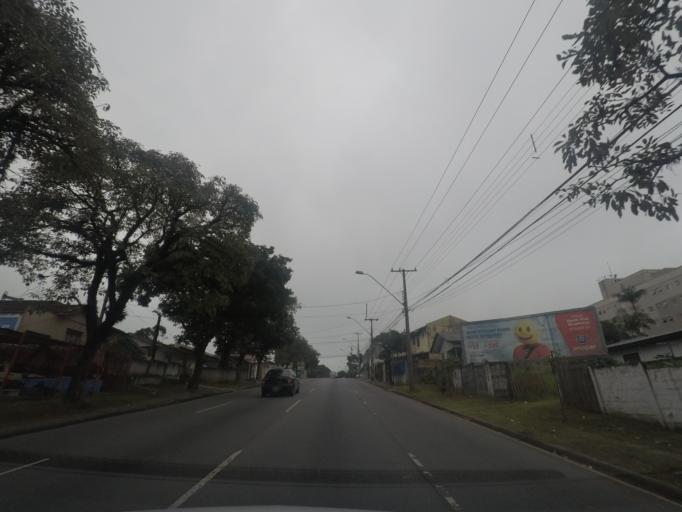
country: BR
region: Parana
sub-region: Curitiba
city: Curitiba
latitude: -25.3809
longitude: -49.2264
